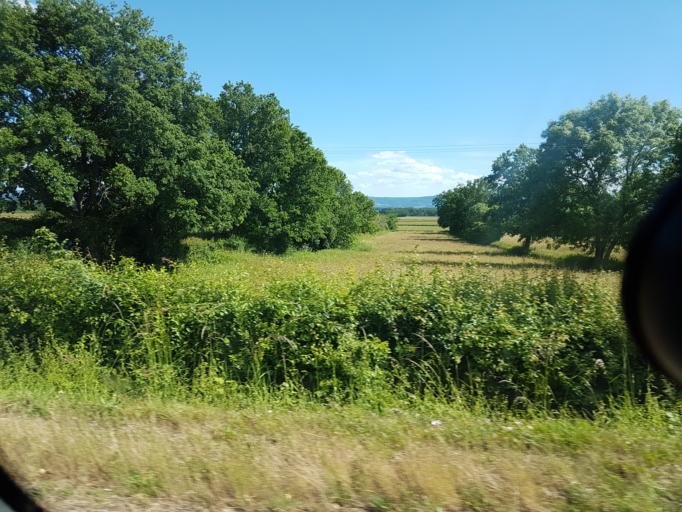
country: FR
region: Bourgogne
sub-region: Departement de Saone-et-Loire
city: Autun
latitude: 47.0517
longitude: 4.3028
